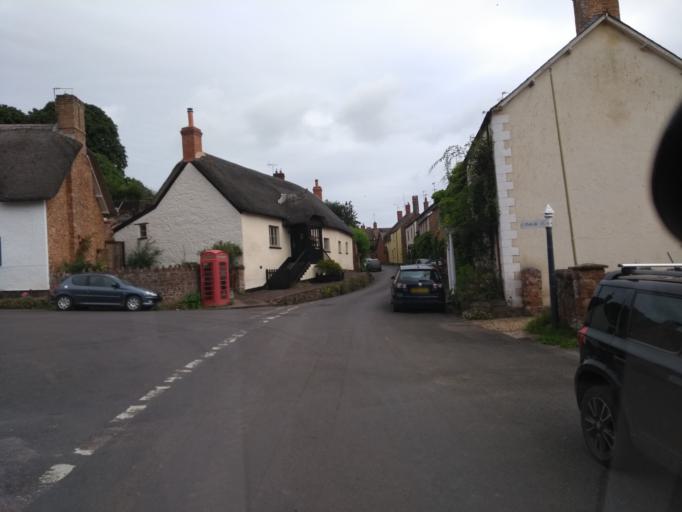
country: GB
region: England
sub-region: Somerset
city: Bishops Lydeard
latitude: 51.0444
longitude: -3.2275
